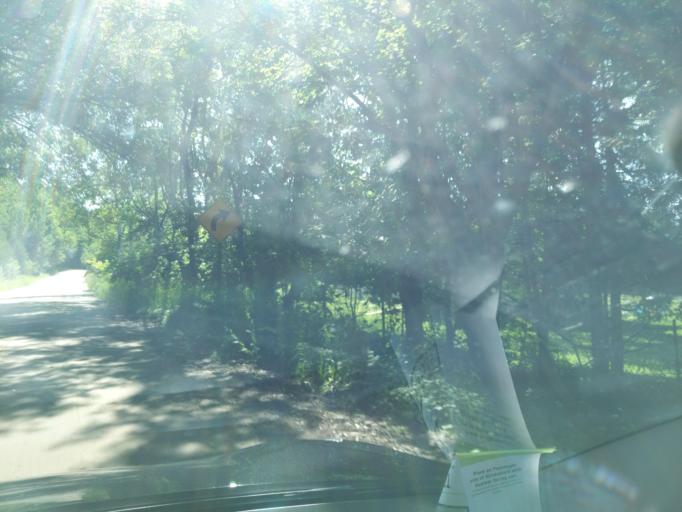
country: US
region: Michigan
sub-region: Cheboygan County
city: Cheboygan
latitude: 45.6501
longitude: -84.6221
